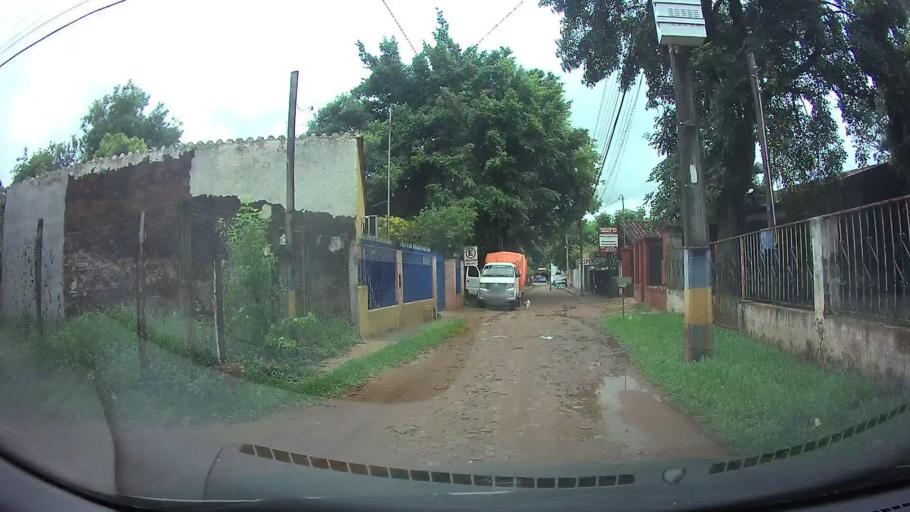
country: PY
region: Central
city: San Lorenzo
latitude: -25.2738
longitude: -57.4848
